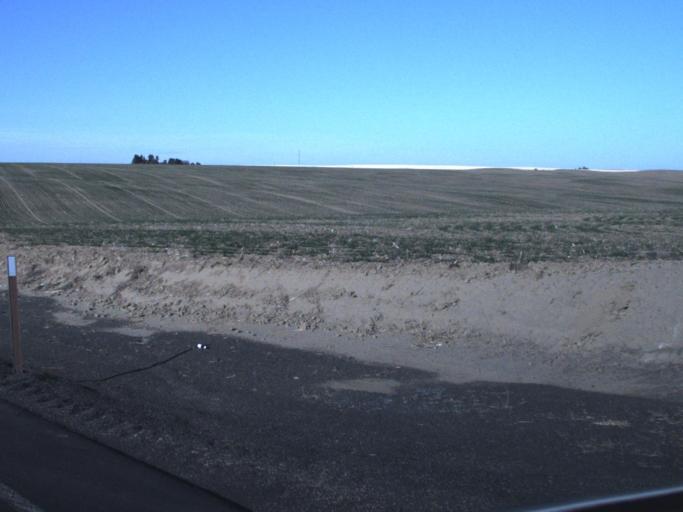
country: US
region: Washington
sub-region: Adams County
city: Ritzville
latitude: 47.0601
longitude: -118.3651
